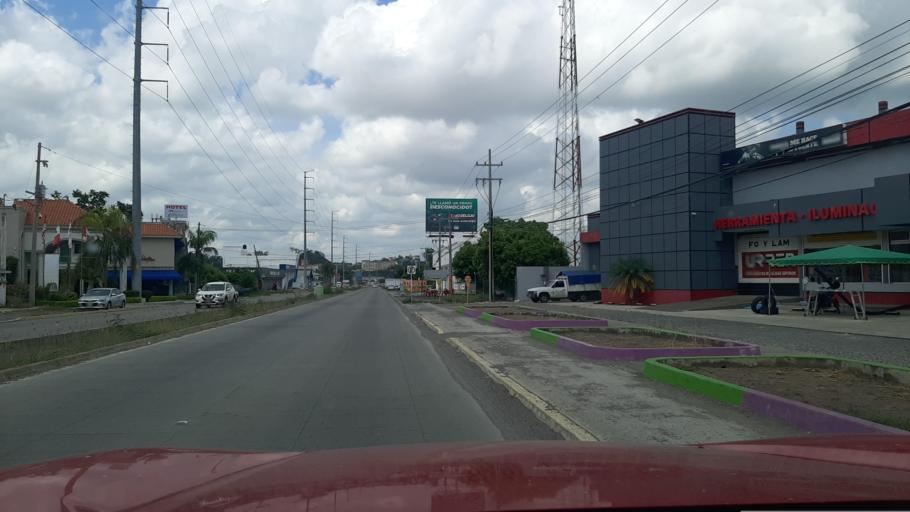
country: MX
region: Veracruz
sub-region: Poza Rica de Hidalgo
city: Villa de las Flores
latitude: 20.5737
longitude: -97.4318
